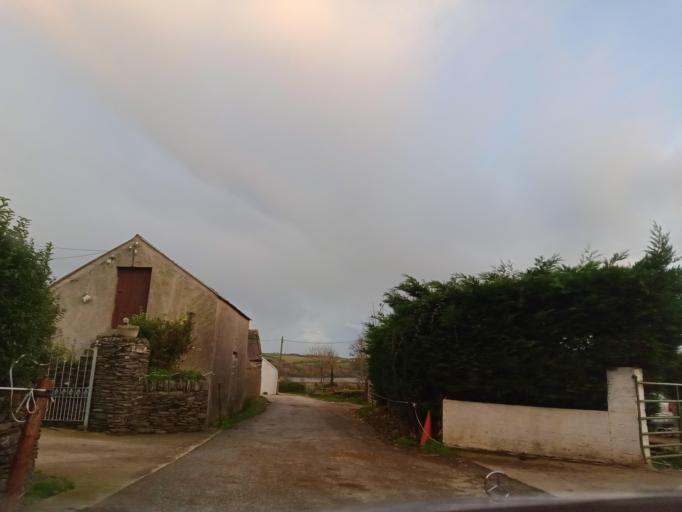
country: IE
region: Leinster
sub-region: Loch Garman
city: New Ross
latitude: 52.3360
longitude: -7.0079
